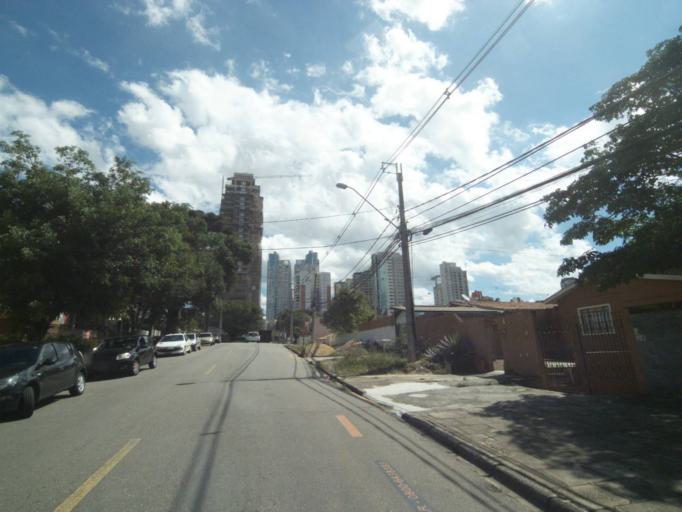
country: BR
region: Parana
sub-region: Curitiba
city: Curitiba
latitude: -25.4363
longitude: -49.3357
